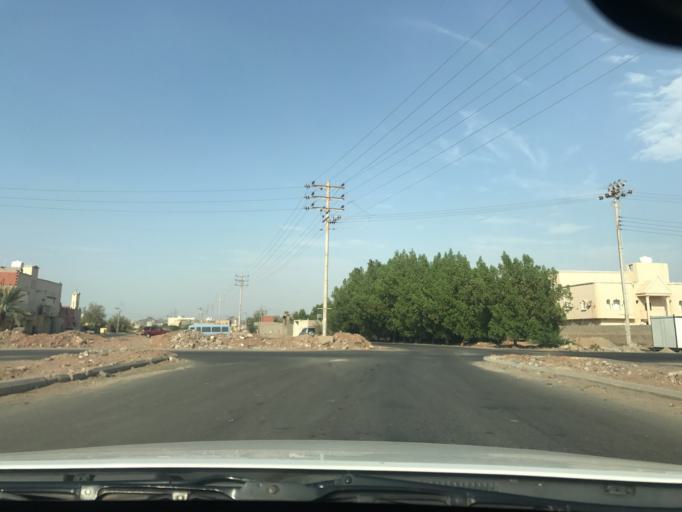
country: SA
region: Makkah
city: Al Jumum
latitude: 21.4545
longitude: 39.5495
